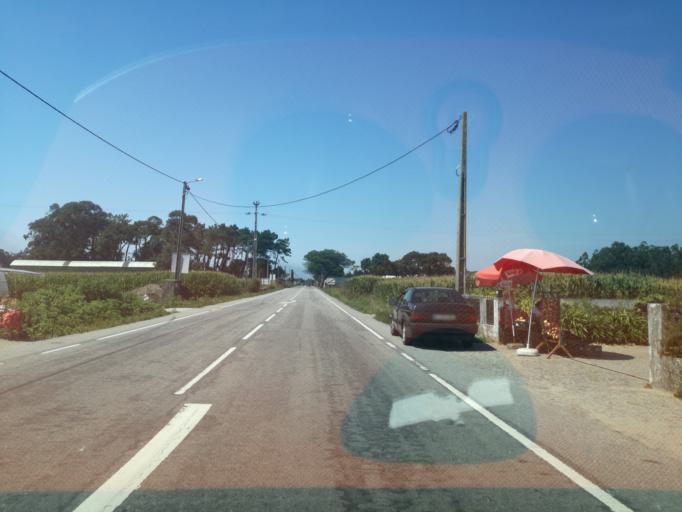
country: PT
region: Braga
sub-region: Esposende
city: Apulia
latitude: 41.4957
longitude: -8.7564
